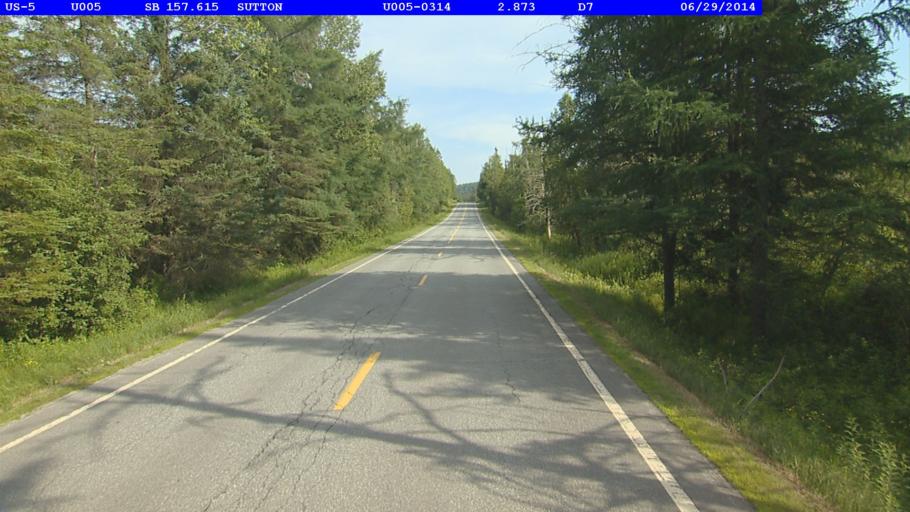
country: US
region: Vermont
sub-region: Caledonia County
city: Lyndonville
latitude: 44.6680
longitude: -72.0253
